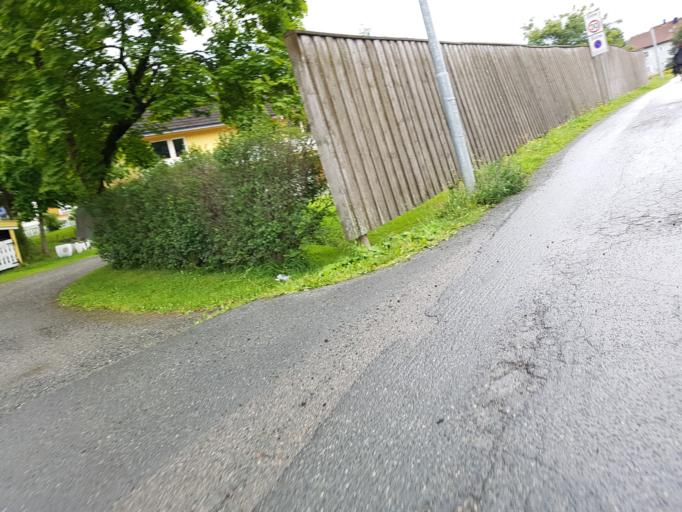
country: NO
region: Sor-Trondelag
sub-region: Trondheim
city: Trondheim
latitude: 63.3963
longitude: 10.4043
